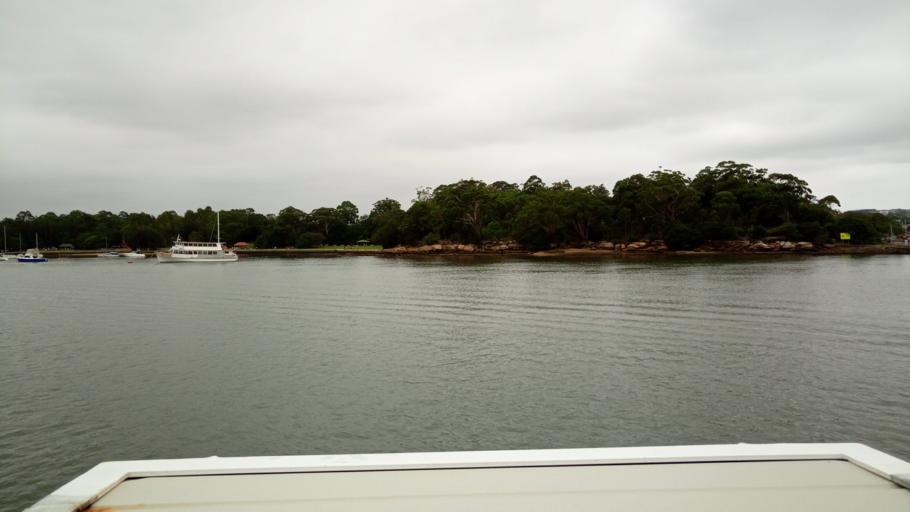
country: AU
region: New South Wales
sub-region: Canada Bay
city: Concord
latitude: -33.8357
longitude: 151.1062
